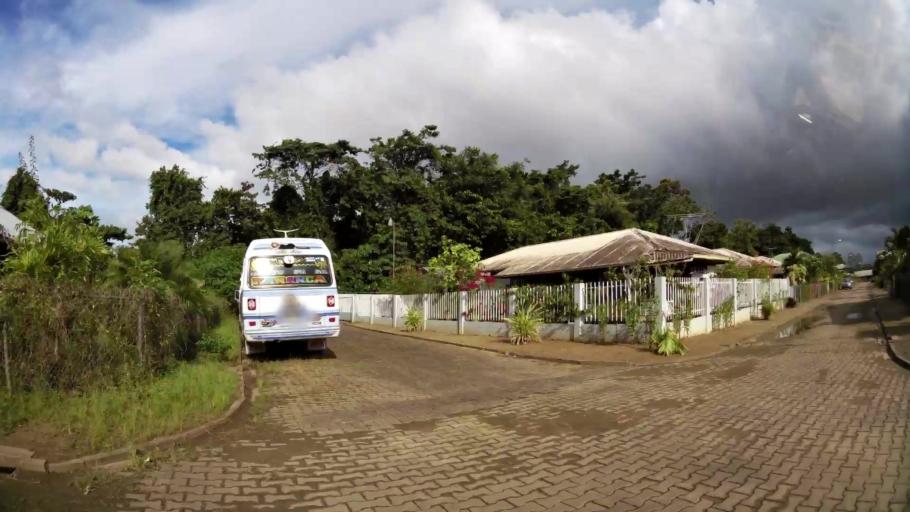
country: SR
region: Paramaribo
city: Paramaribo
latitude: 5.8462
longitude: -55.2112
